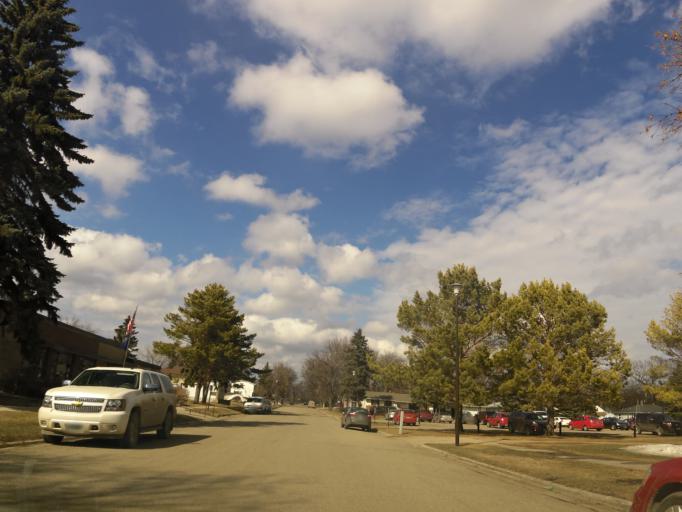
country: US
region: North Dakota
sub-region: Walsh County
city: Grafton
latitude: 48.4207
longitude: -97.3996
